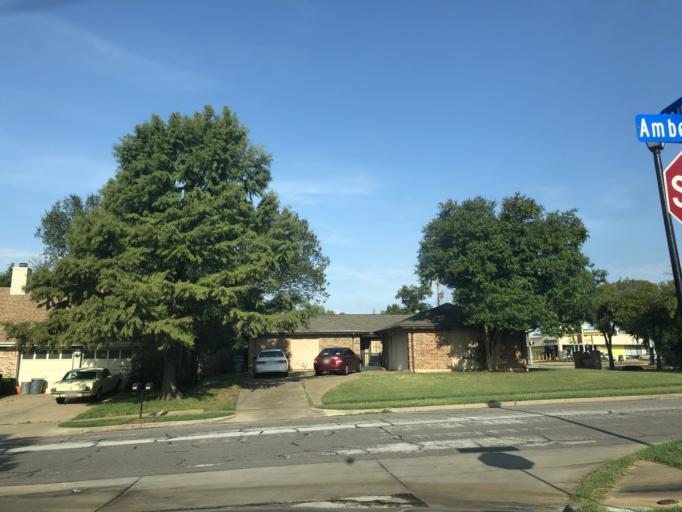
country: US
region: Texas
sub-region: Tarrant County
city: Euless
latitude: 32.8718
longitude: -97.0822
